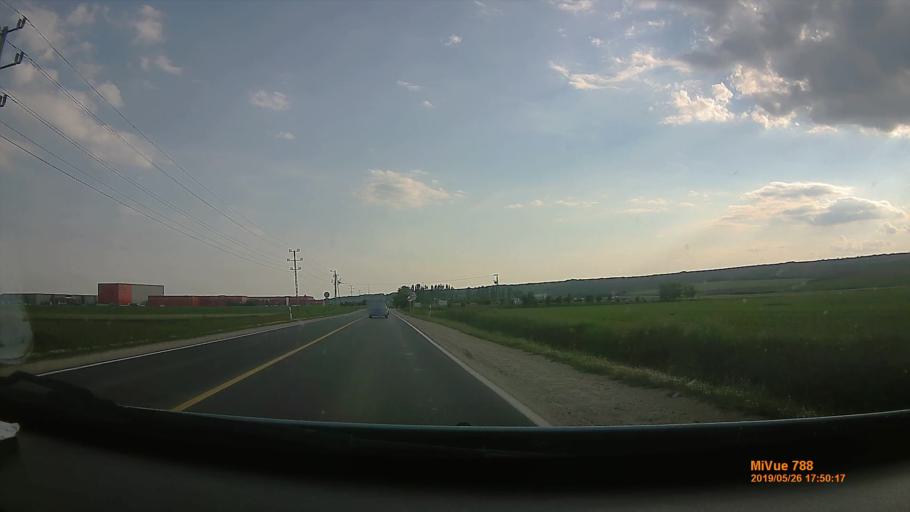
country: HU
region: Borsod-Abauj-Zemplen
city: Szikszo
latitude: 48.1833
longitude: 20.9205
